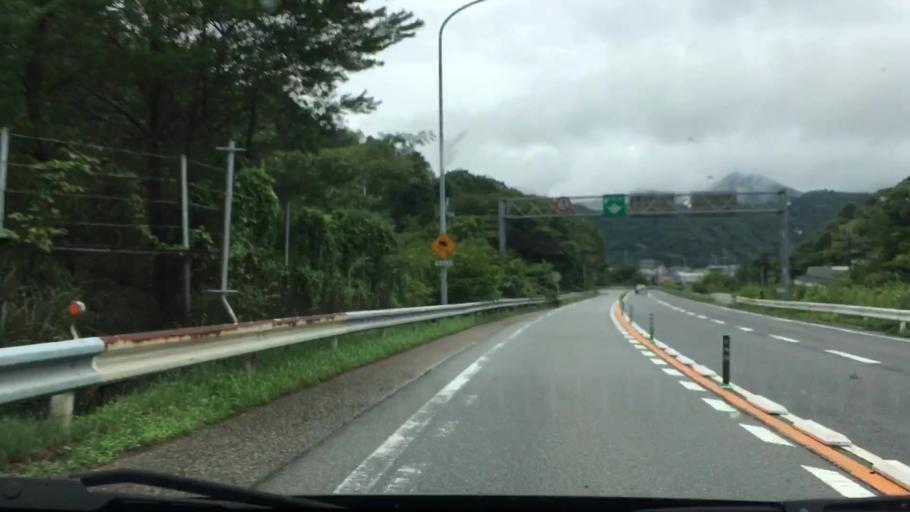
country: JP
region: Hyogo
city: Himeji
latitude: 35.0162
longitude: 134.7645
